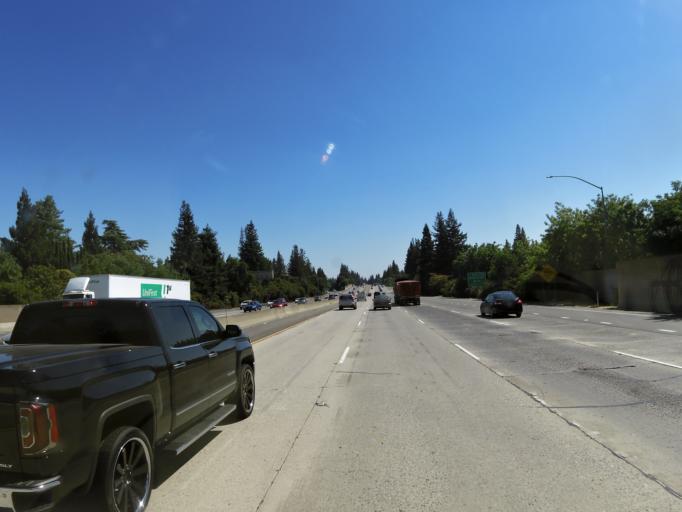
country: US
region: California
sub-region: Yolo County
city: West Sacramento
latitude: 38.5223
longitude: -121.5218
